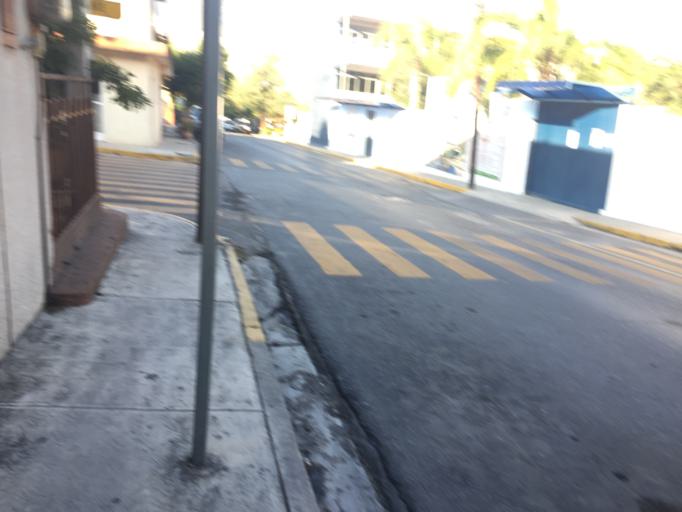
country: MX
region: Nuevo Leon
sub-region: San Pedro Garza Garcia
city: San Pedro Garza Garcia
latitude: 25.6598
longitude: -100.4027
